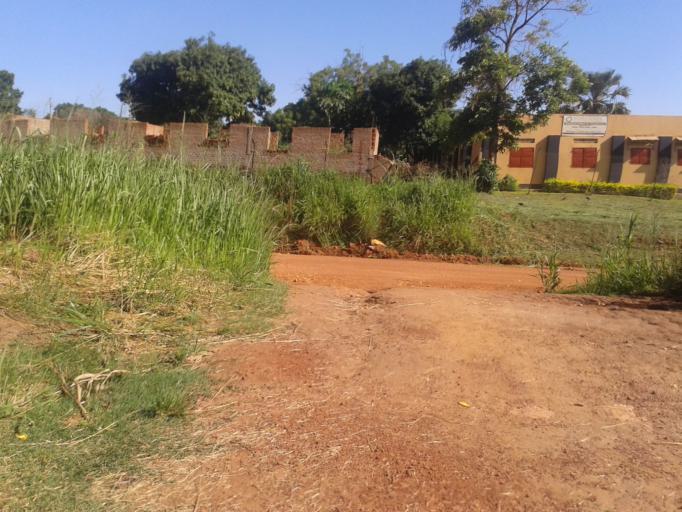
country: UG
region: Northern Region
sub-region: Gulu District
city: Gulu
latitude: 2.7905
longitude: 32.3059
